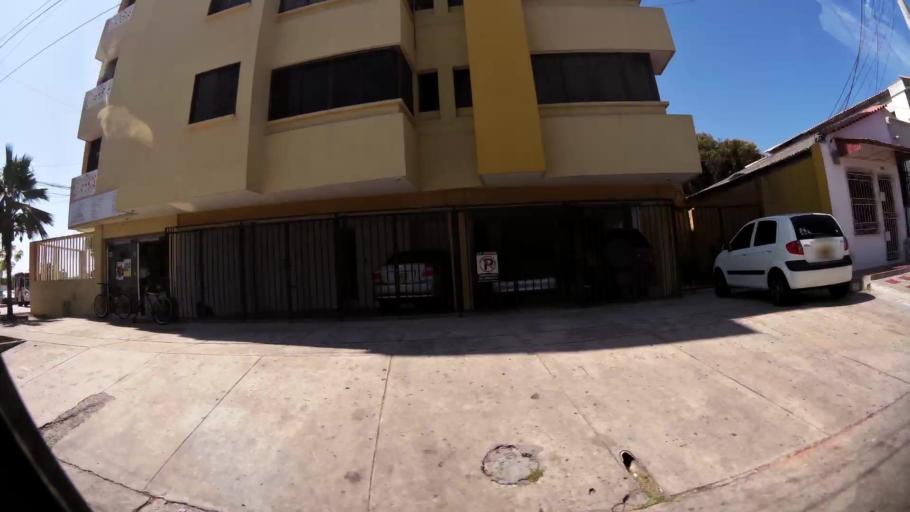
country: CO
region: Atlantico
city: Barranquilla
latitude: 11.0040
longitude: -74.7953
